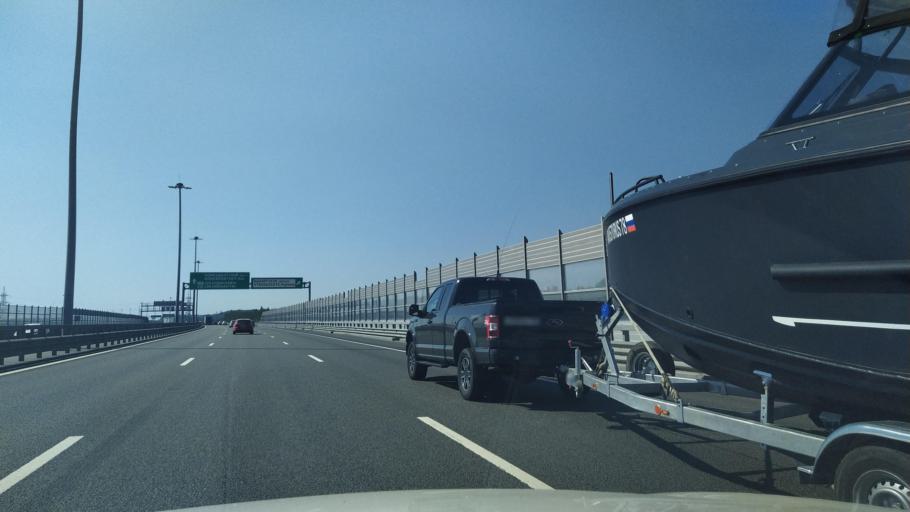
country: RU
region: St.-Petersburg
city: Pargolovo
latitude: 60.0981
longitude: 30.2977
